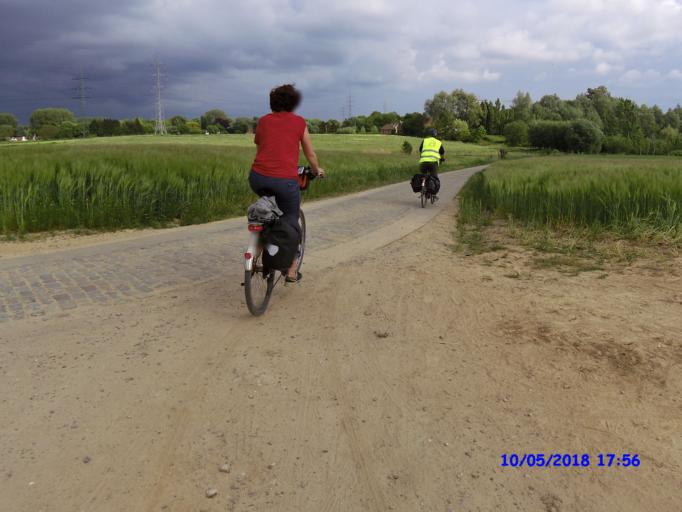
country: BE
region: Flanders
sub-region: Provincie Vlaams-Brabant
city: Dilbeek
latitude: 50.8253
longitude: 4.2547
